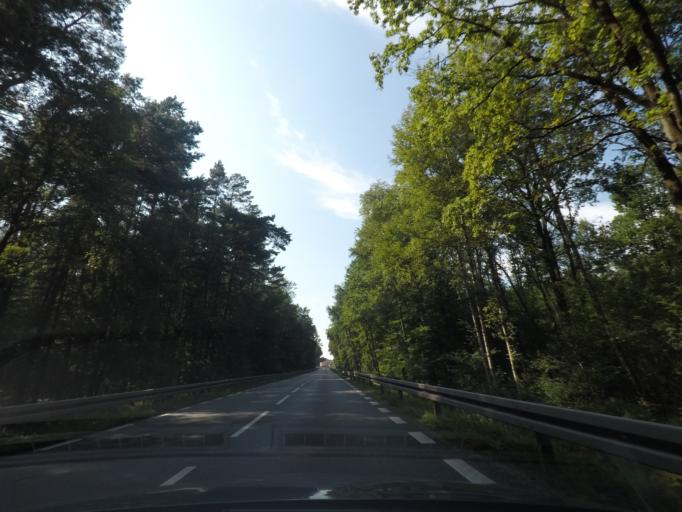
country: PL
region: Silesian Voivodeship
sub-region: Powiat pszczynski
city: Kryry
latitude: 50.0240
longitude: 18.8395
